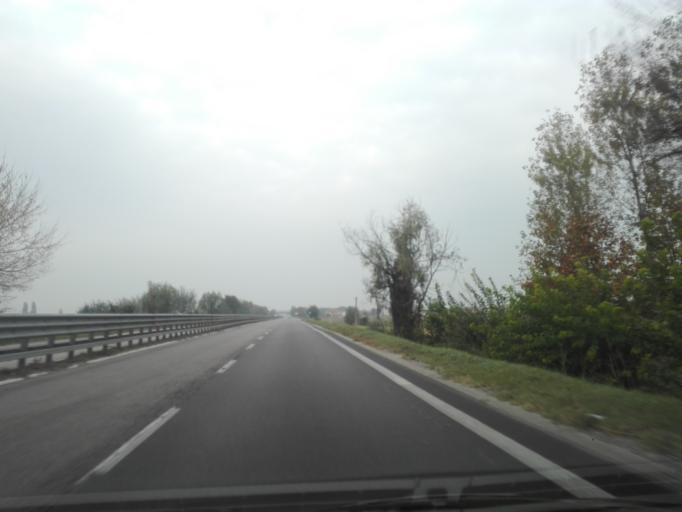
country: IT
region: Veneto
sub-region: Provincia di Verona
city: Spinimbecco
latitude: 45.1334
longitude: 11.3679
